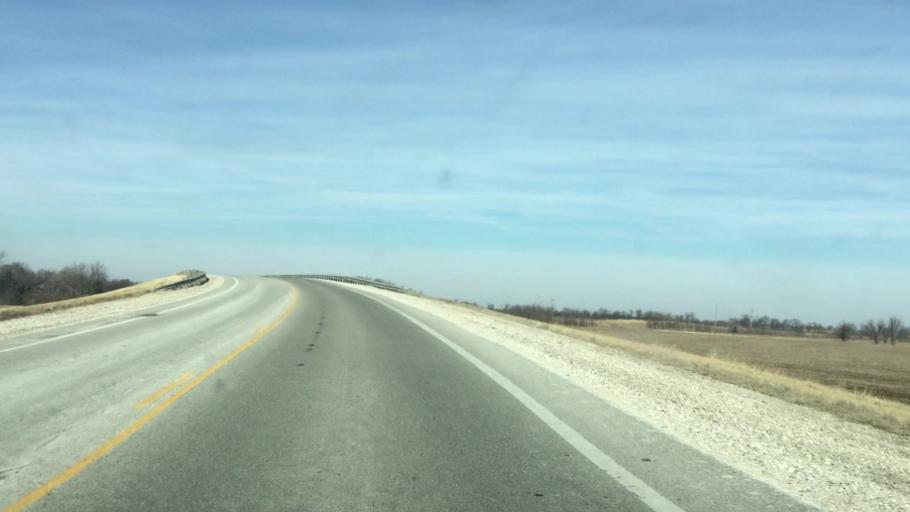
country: US
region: Kansas
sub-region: Labette County
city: Parsons
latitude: 37.3808
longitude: -95.2593
